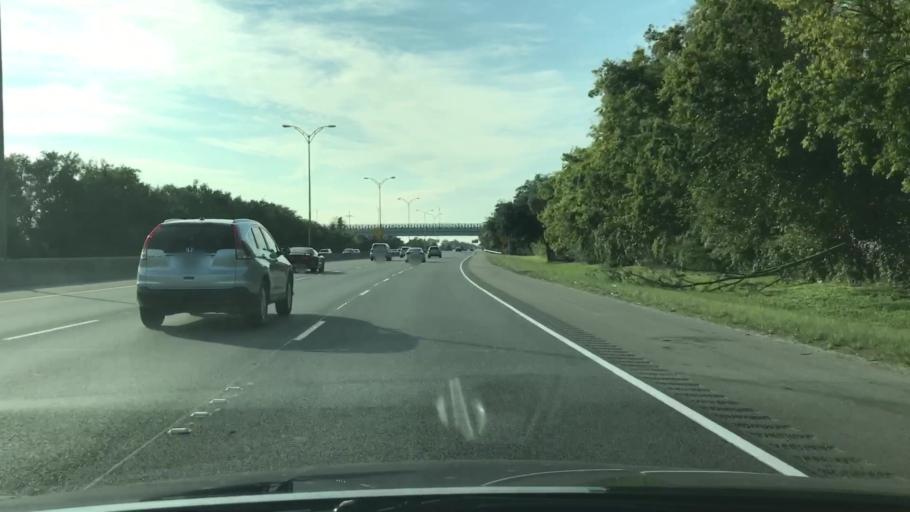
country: US
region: Louisiana
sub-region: Orleans Parish
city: New Orleans
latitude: 29.9929
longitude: -90.0830
